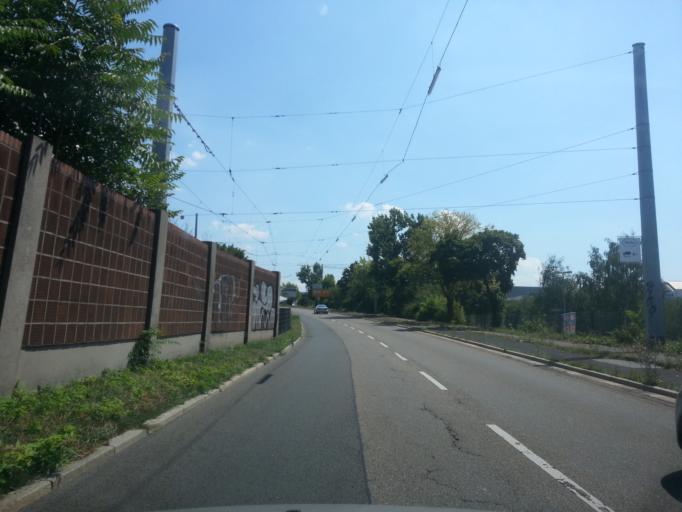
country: DE
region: Baden-Wuerttemberg
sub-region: Karlsruhe Region
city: Mannheim
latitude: 49.5363
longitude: 8.4725
